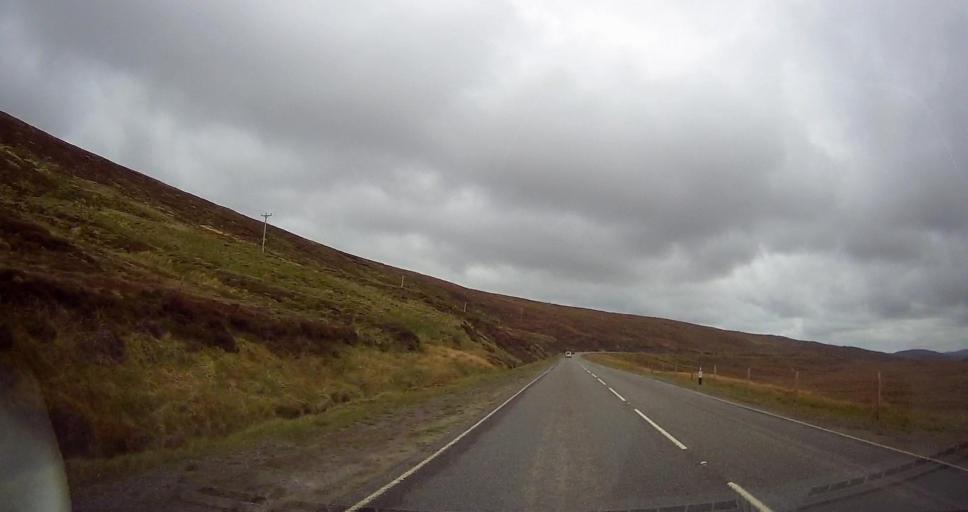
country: GB
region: Scotland
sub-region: Shetland Islands
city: Lerwick
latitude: 60.3083
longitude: -1.2441
